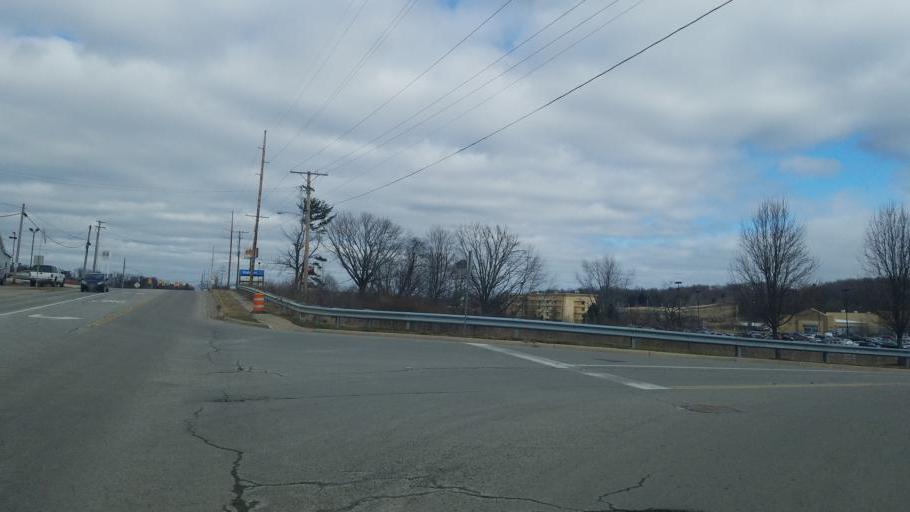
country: US
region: Ohio
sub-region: Richland County
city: Mansfield
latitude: 40.6905
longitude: -82.5113
